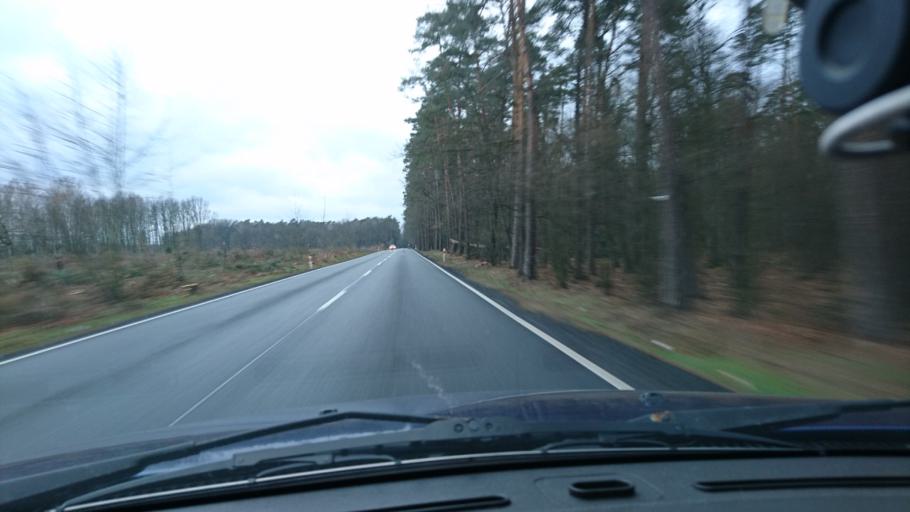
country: PL
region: Opole Voivodeship
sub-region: Powiat oleski
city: Olesno
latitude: 50.9396
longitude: 18.3270
